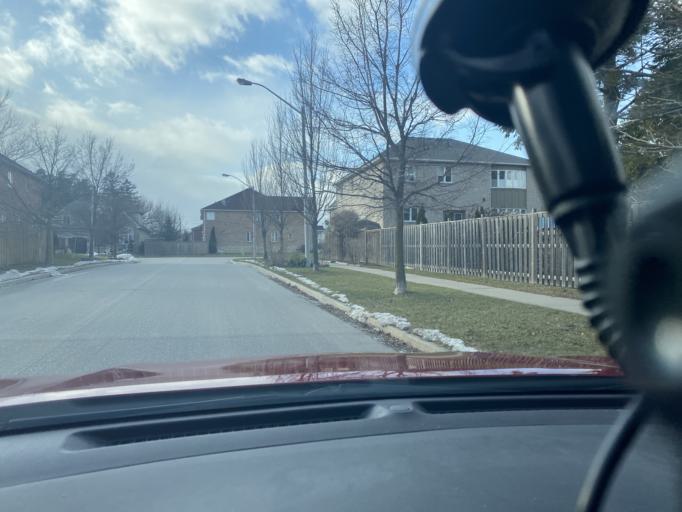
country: CA
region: Ontario
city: Scarborough
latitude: 43.7960
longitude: -79.1726
